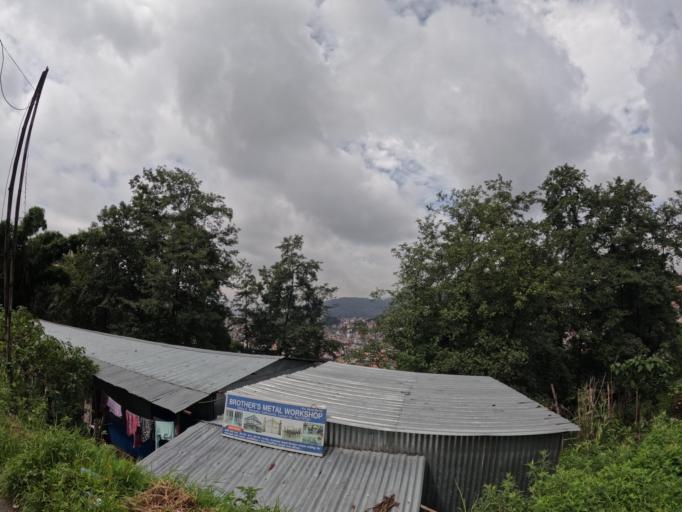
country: NP
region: Central Region
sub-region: Bagmati Zone
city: Kathmandu
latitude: 27.7513
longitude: 85.3200
